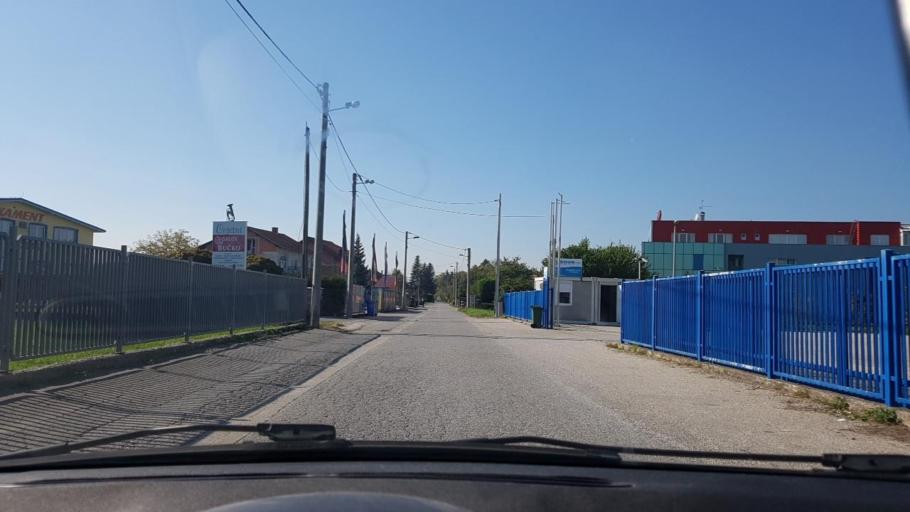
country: HR
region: Grad Zagreb
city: Lucko
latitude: 45.7582
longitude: 15.8899
